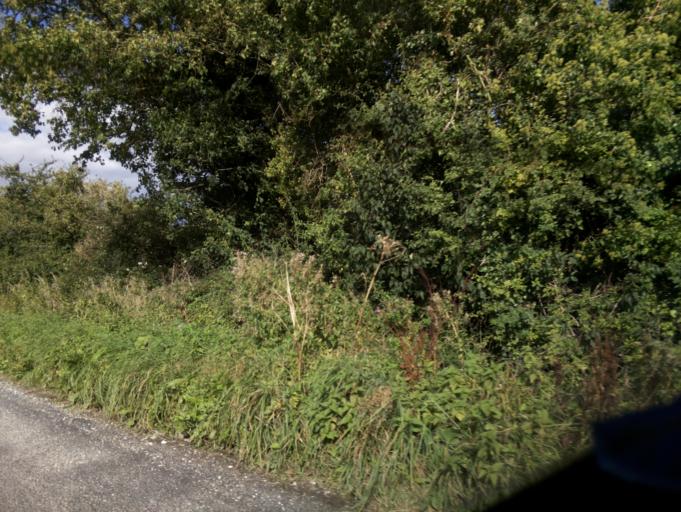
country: GB
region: England
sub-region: Hampshire
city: Winchester
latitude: 51.0753
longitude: -1.3805
